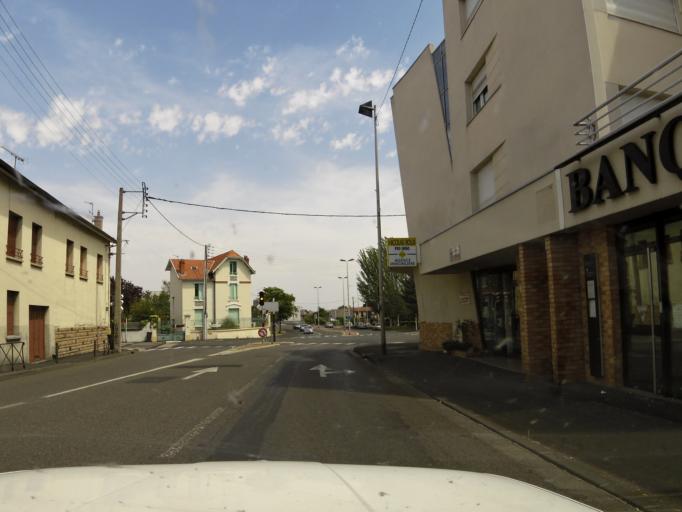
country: FR
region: Auvergne
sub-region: Departement du Puy-de-Dome
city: Beaumont
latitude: 45.7533
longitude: 3.0874
